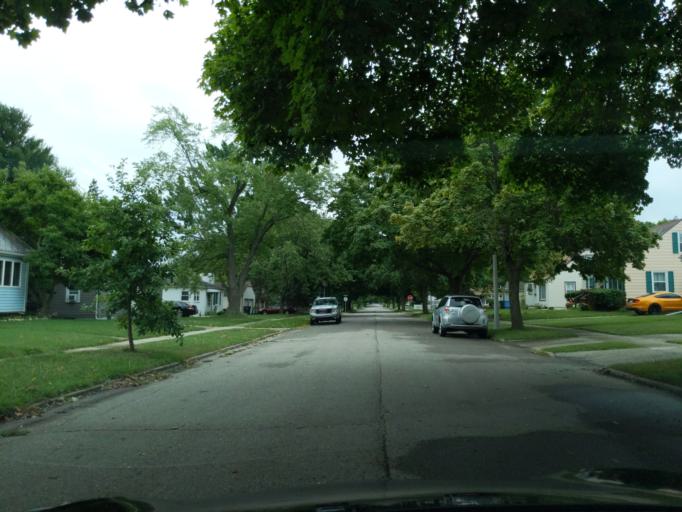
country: US
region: Michigan
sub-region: Ingham County
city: Lansing
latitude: 42.6932
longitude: -84.5367
